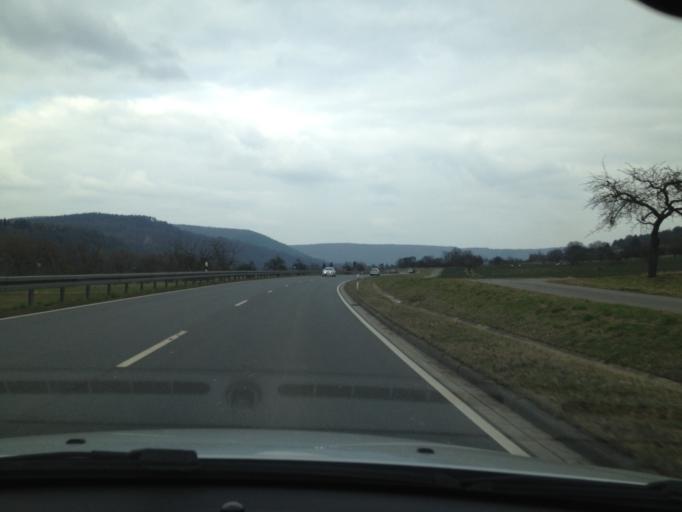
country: DE
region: Bavaria
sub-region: Regierungsbezirk Unterfranken
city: Stadtprozelten
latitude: 49.7733
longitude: 9.4033
